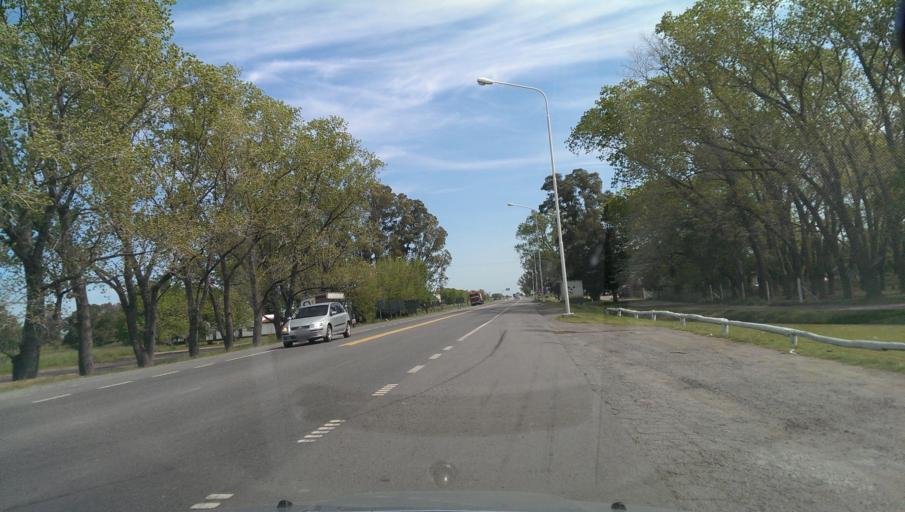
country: AR
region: Buenos Aires
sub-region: Partido de Azul
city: Azul
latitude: -36.3880
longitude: -59.4929
